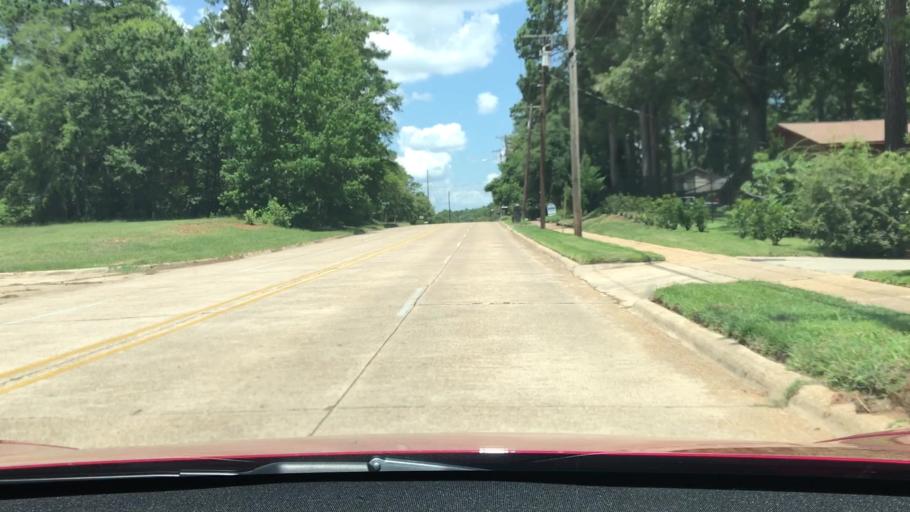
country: US
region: Louisiana
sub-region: Bossier Parish
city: Bossier City
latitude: 32.4393
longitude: -93.7355
